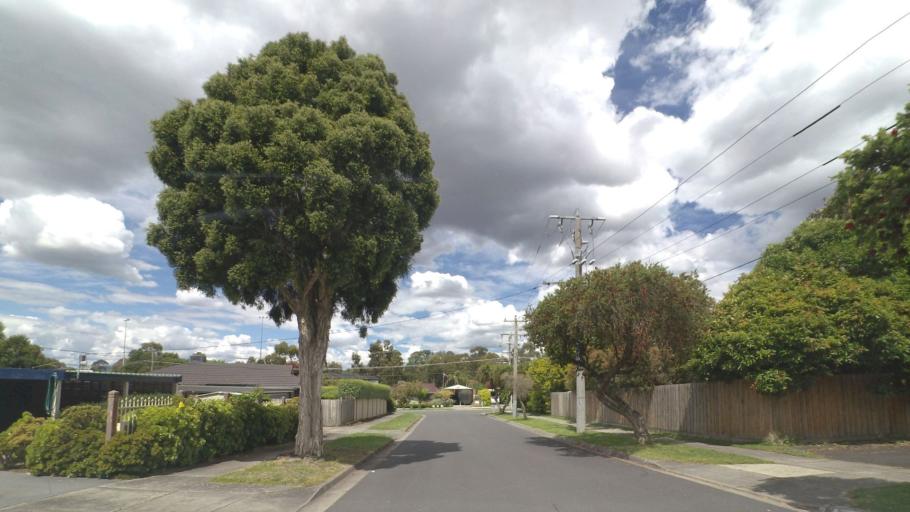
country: AU
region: Victoria
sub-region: Knox
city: Wantirna
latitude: -37.8487
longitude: 145.2353
